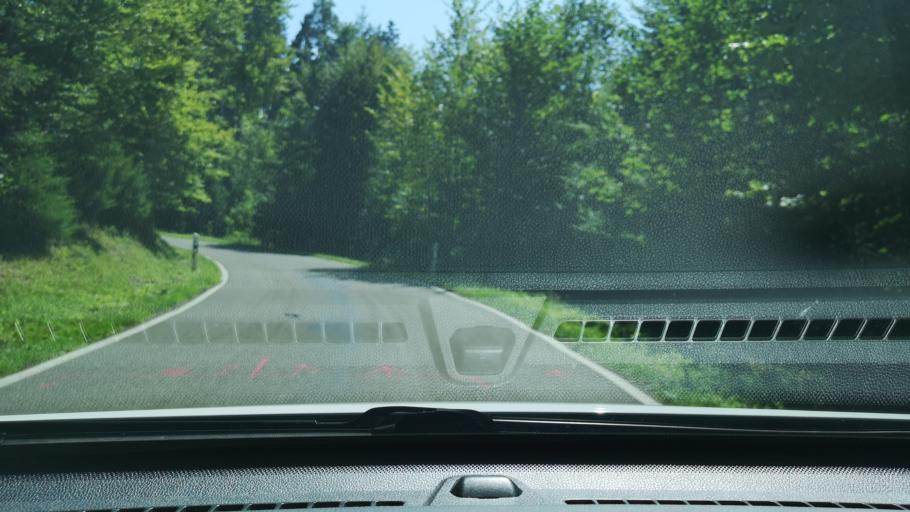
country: DE
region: Baden-Wuerttemberg
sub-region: Freiburg Region
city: Muhlheim am Bach
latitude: 48.3551
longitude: 8.7149
